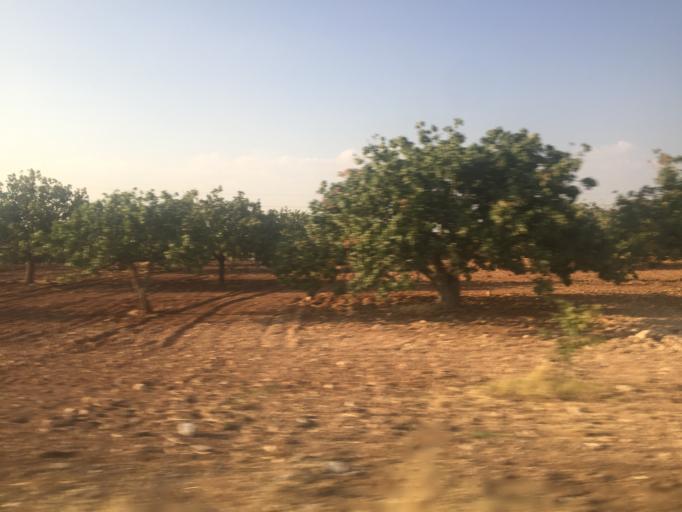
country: TR
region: Gaziantep
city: Nizip
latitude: 37.0142
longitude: 37.8477
